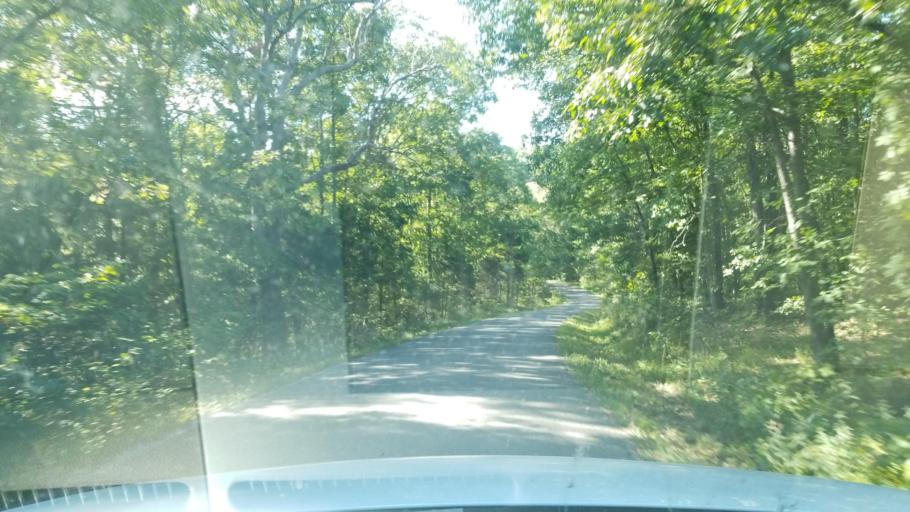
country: US
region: Illinois
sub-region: Hardin County
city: Elizabethtown
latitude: 37.6012
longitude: -88.3818
